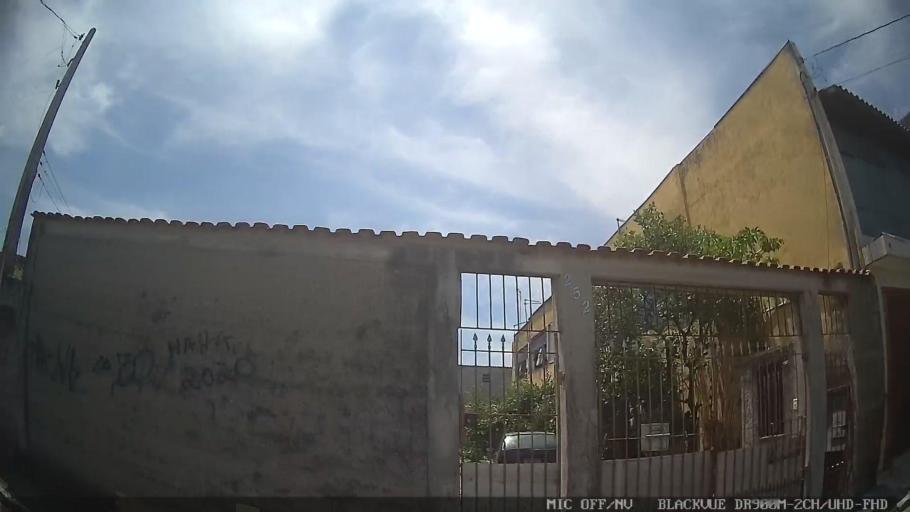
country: BR
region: Sao Paulo
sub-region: Suzano
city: Suzano
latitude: -23.5297
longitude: -46.3127
